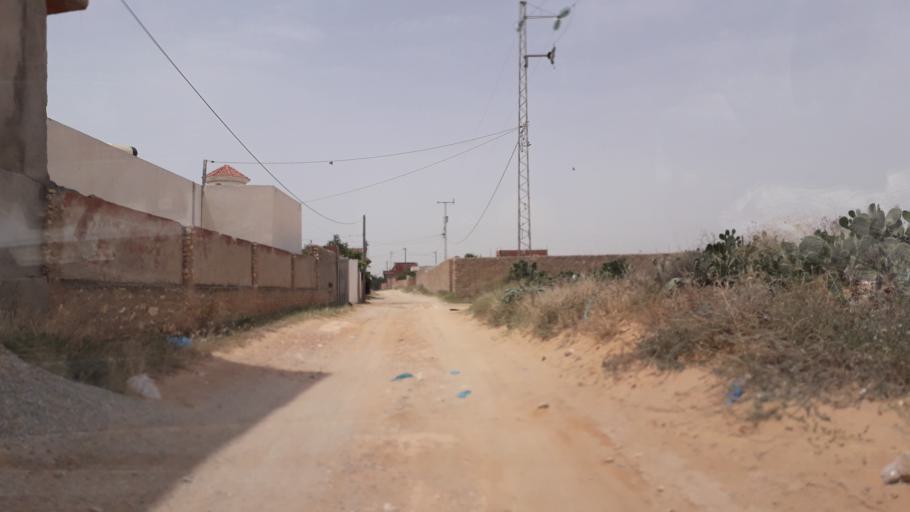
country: TN
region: Safaqis
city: Al Qarmadah
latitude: 34.8547
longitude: 10.7604
